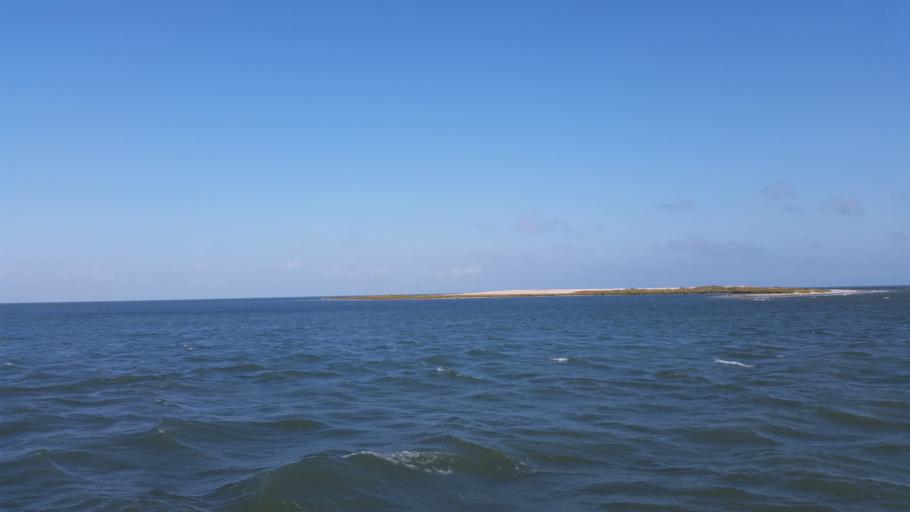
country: US
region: North Carolina
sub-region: Dare County
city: Buxton
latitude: 35.2130
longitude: -75.7141
